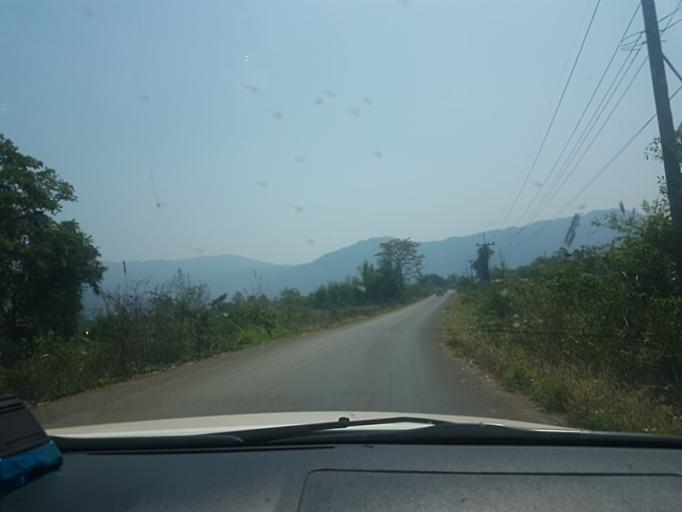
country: LA
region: Bolikhamxai
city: Ban Nahin
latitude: 18.5329
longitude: 104.4761
